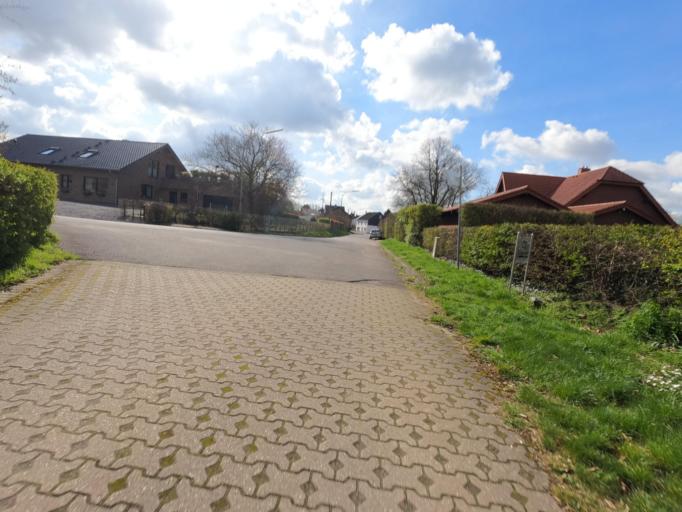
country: DE
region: North Rhine-Westphalia
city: Erkelenz
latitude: 51.0277
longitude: 6.3478
